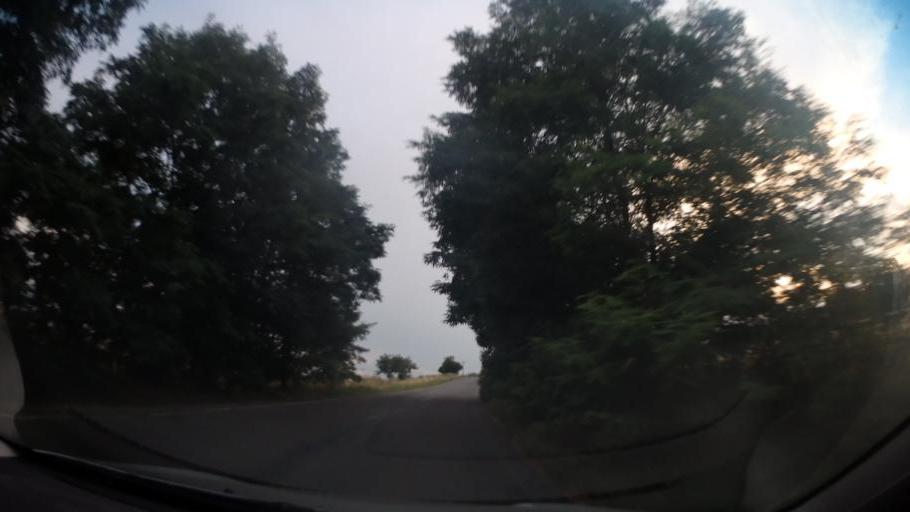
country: CZ
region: South Moravian
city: Dolni Kounice
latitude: 49.0726
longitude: 16.4894
